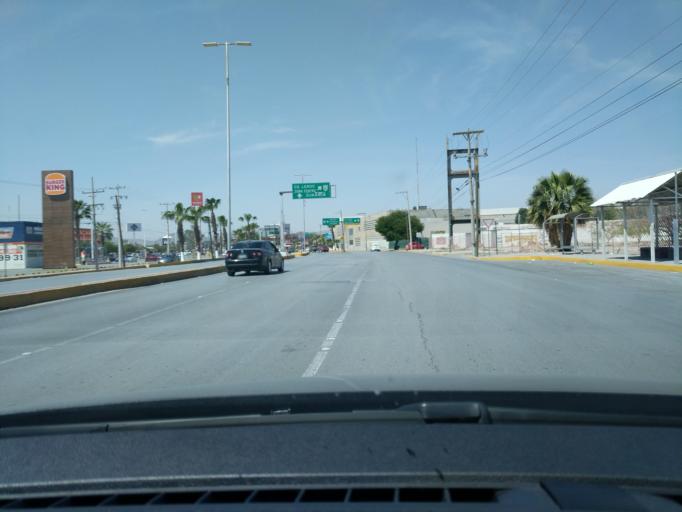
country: MX
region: Durango
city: Gomez Palacio
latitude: 25.5555
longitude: -103.5042
